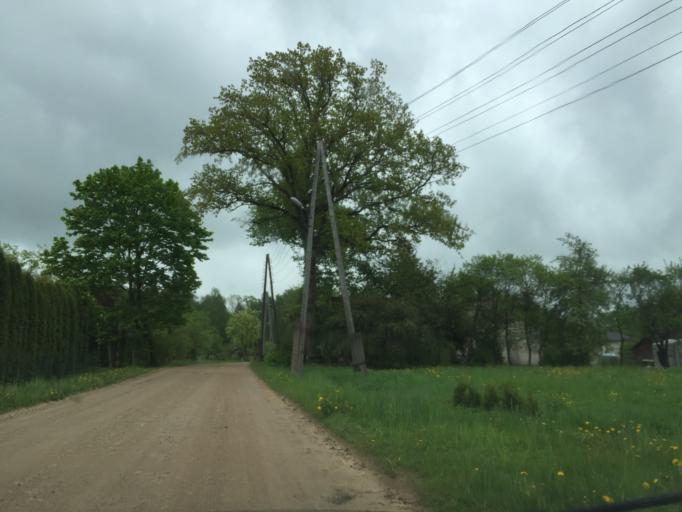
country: LV
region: Lielvarde
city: Lielvarde
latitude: 56.7278
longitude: 24.7889
